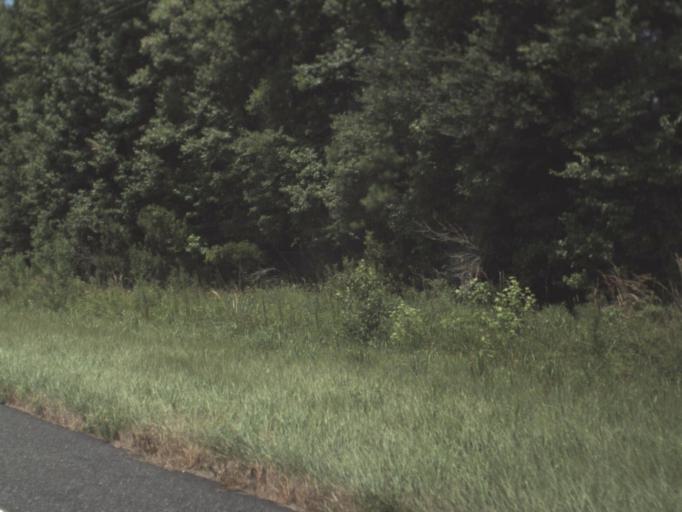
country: US
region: Florida
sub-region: Taylor County
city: Perry
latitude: 30.2742
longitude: -83.7216
